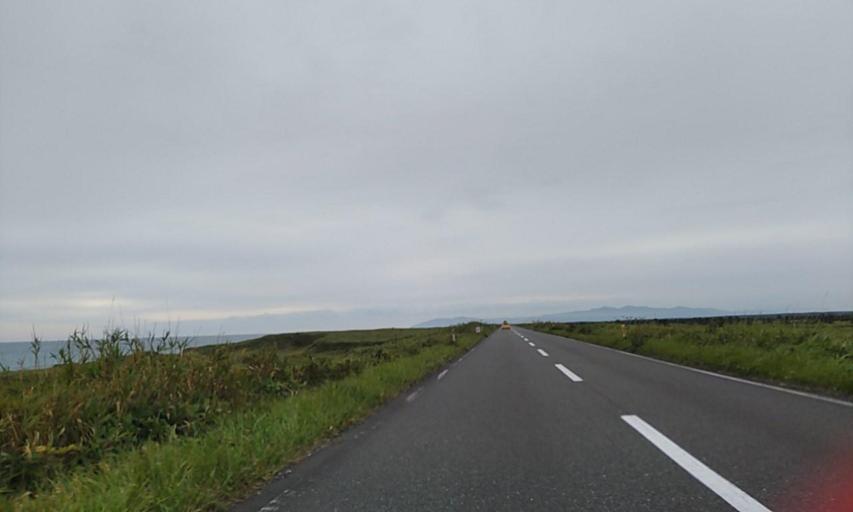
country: JP
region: Hokkaido
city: Makubetsu
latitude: 45.2680
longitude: 142.2391
